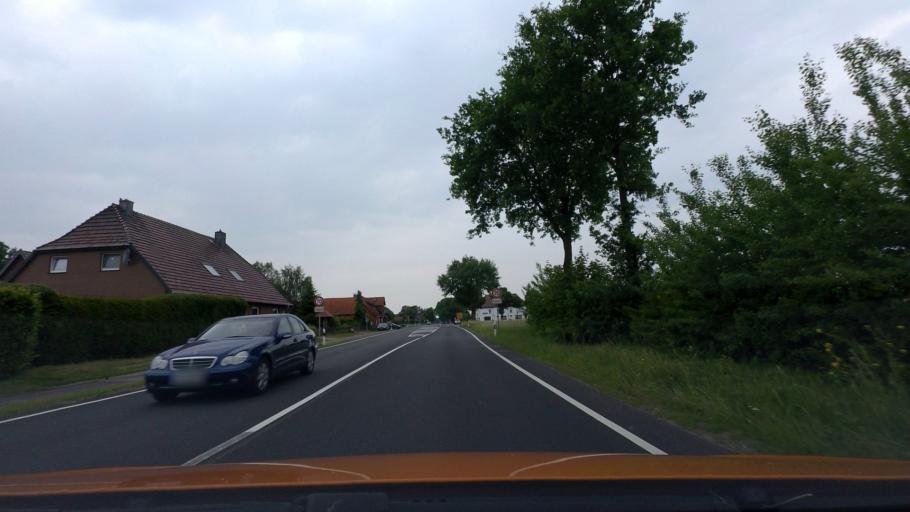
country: DE
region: Lower Saxony
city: Wietzen
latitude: 52.7257
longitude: 9.0468
